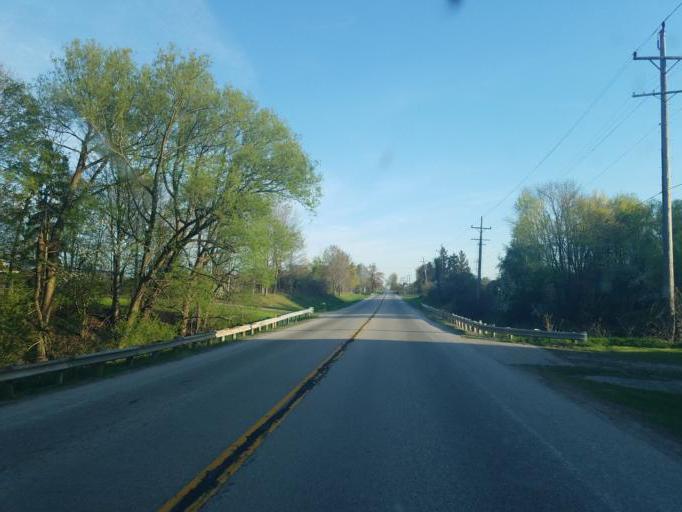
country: US
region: Ohio
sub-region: Ashtabula County
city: Conneaut
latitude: 41.7985
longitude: -80.5721
